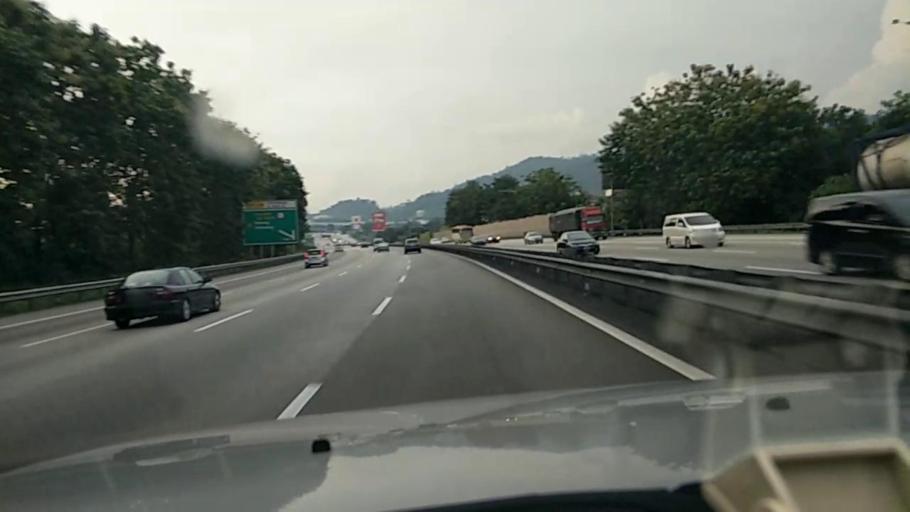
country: MY
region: Selangor
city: Kuang
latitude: 3.2120
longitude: 101.5825
